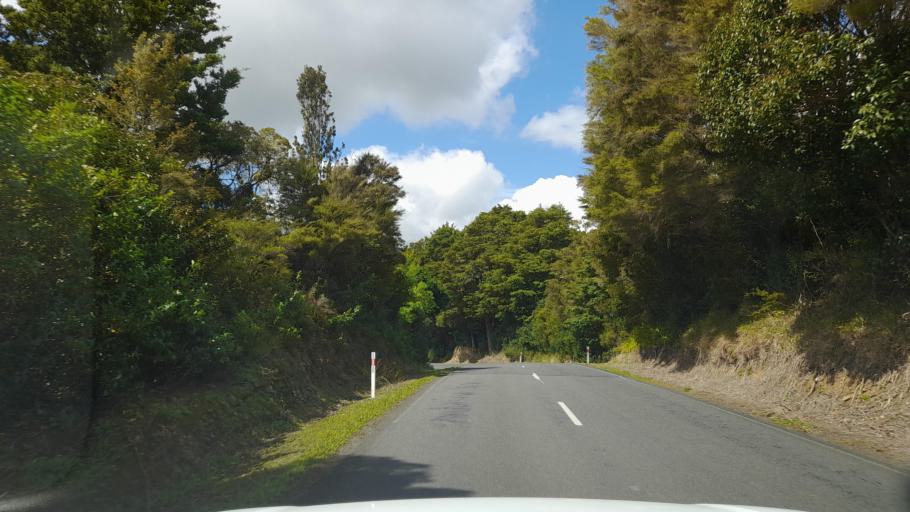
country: NZ
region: Northland
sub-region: Whangarei
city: Maungatapere
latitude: -35.6316
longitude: 174.0775
